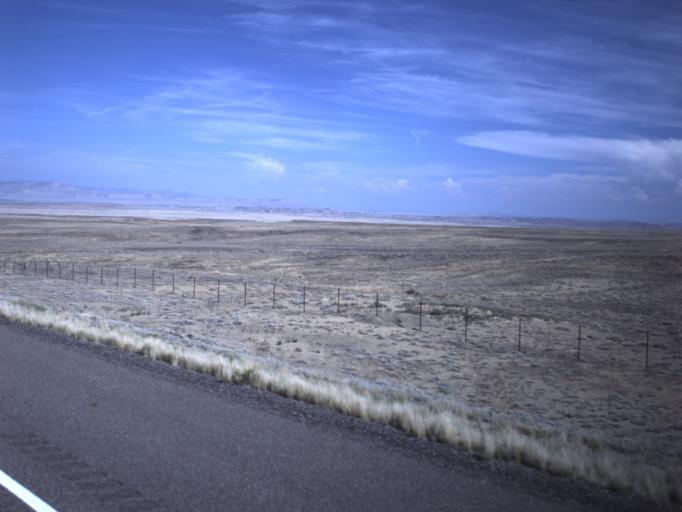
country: US
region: Utah
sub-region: Carbon County
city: East Carbon City
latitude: 38.9430
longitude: -110.3294
